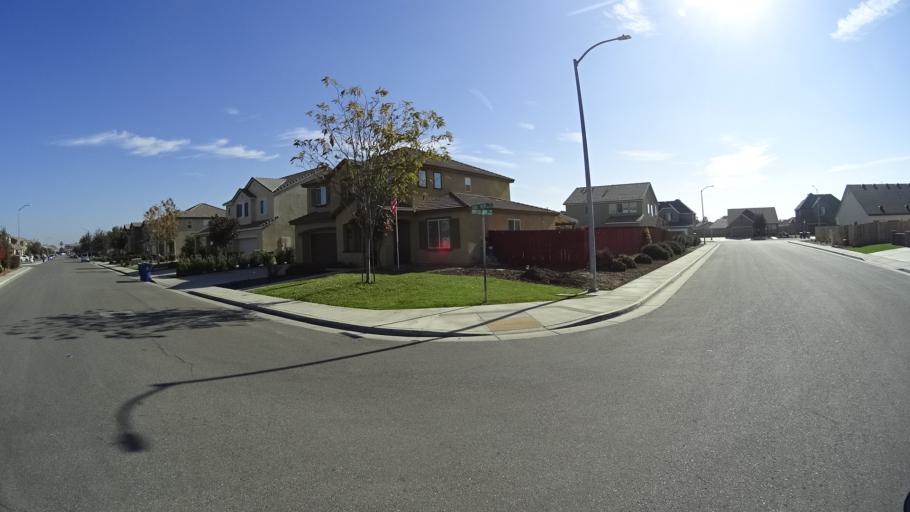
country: US
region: California
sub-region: Kern County
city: Greenfield
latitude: 35.2859
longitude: -119.0616
